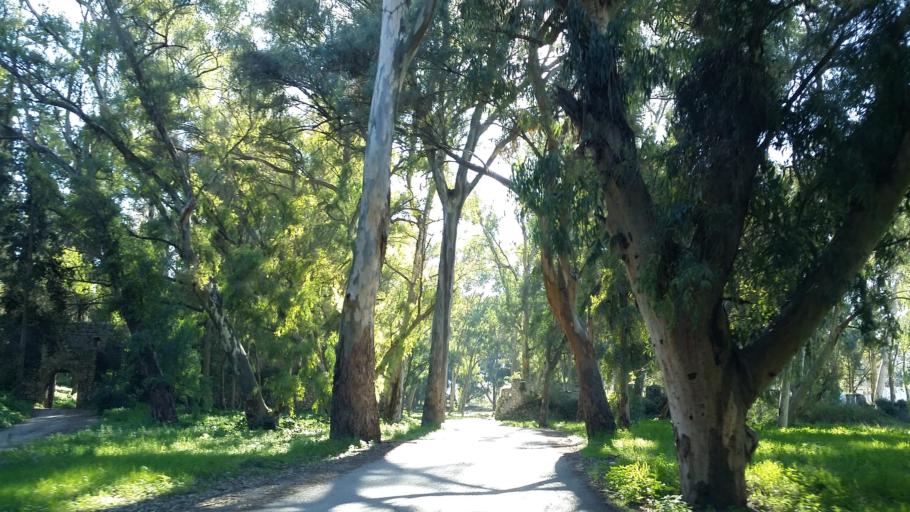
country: GR
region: West Greece
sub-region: Nomos Aitolias kai Akarnanias
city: Vonitsa
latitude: 38.9213
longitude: 20.8822
